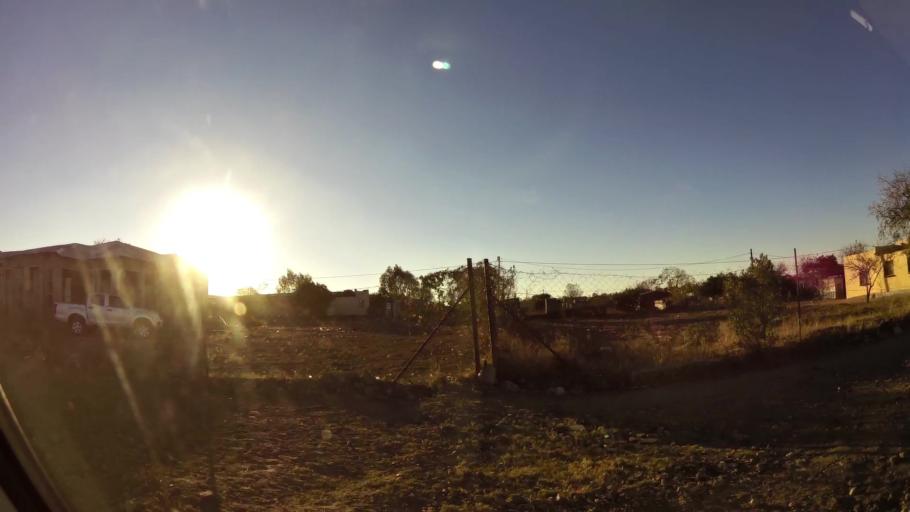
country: ZA
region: Limpopo
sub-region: Capricorn District Municipality
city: Polokwane
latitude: -23.8195
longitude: 29.3775
